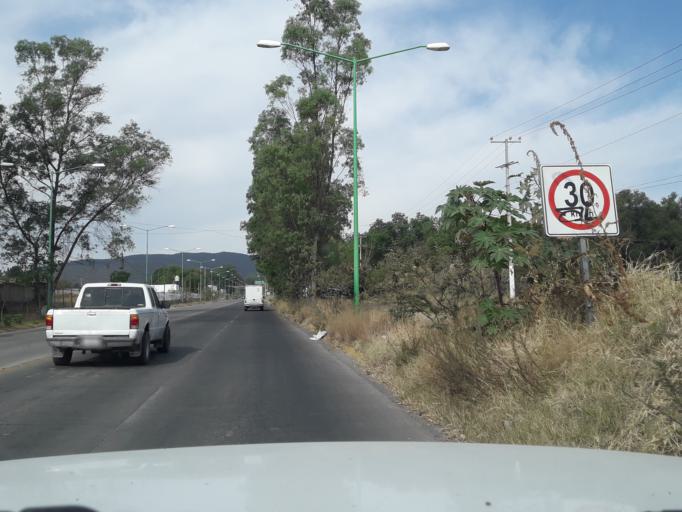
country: MX
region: Jalisco
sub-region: Tlajomulco de Zuniga
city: Palomar
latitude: 20.6206
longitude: -103.4764
